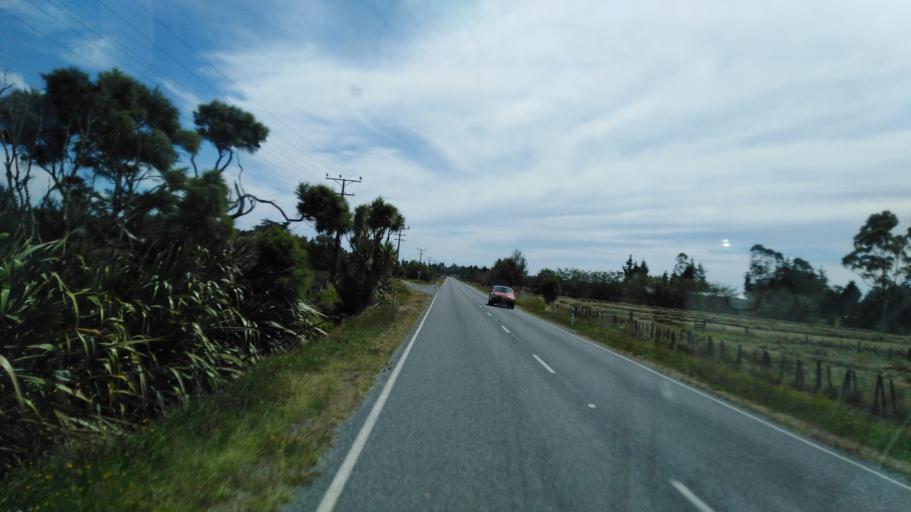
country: NZ
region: West Coast
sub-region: Buller District
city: Westport
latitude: -41.7411
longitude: 171.7112
